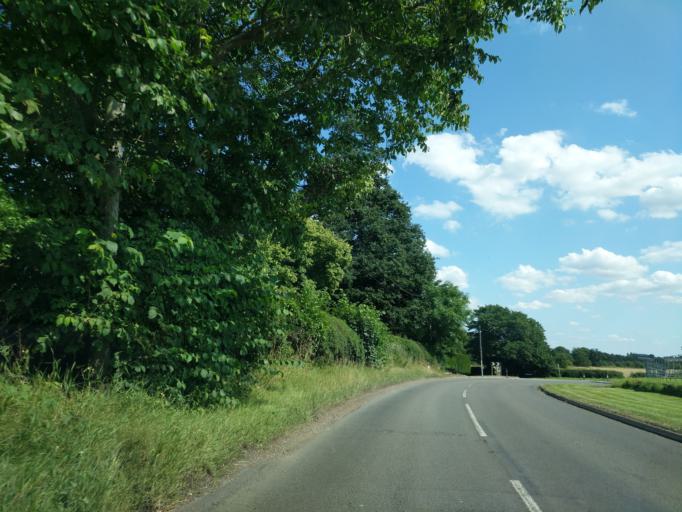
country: GB
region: England
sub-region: Staffordshire
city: Rugeley
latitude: 52.7828
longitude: -1.9358
